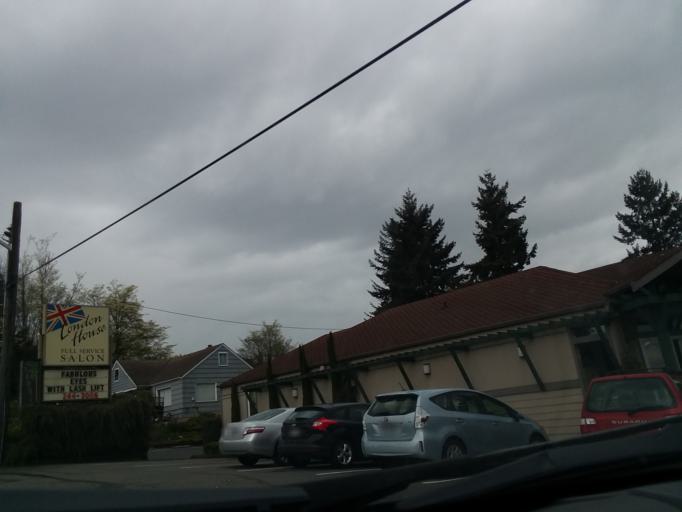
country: US
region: Washington
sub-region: King County
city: Boulevard Park
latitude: 47.4859
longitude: -122.3338
